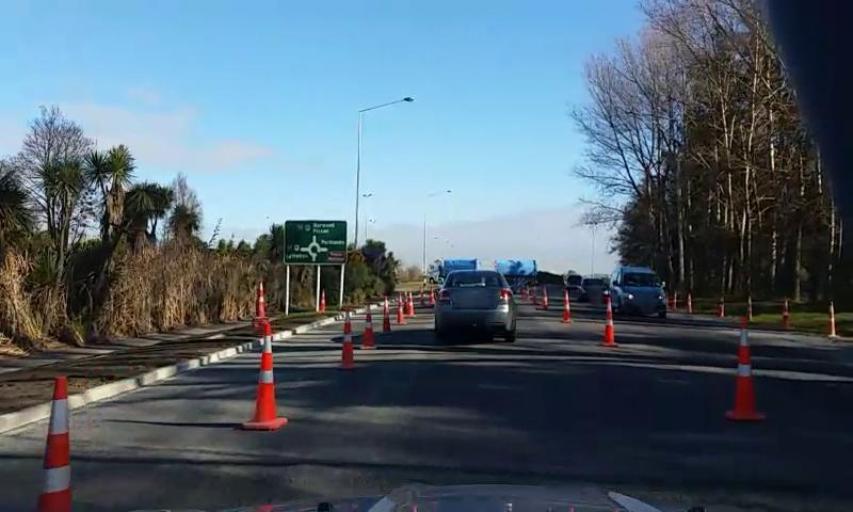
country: NZ
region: Canterbury
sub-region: Christchurch City
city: Christchurch
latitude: -43.4936
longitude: 172.7037
